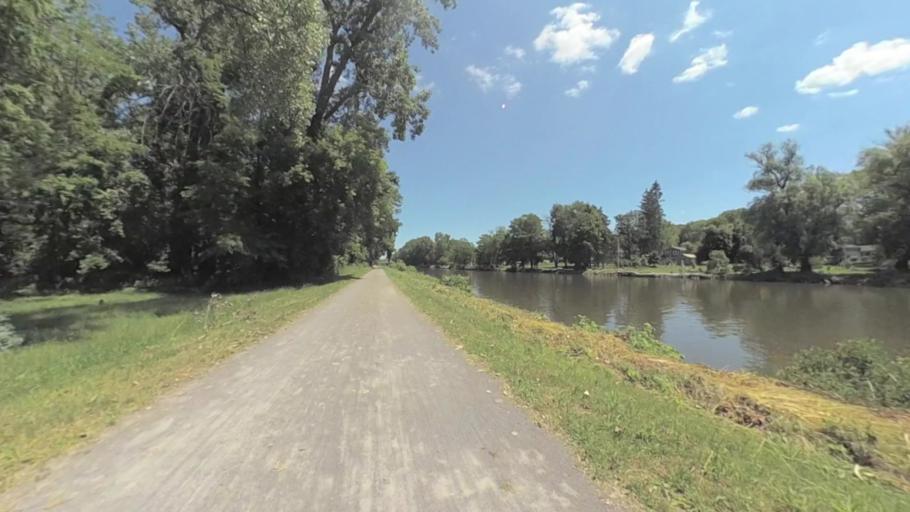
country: US
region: New York
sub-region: Monroe County
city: Fairport
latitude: 43.0691
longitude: -77.4683
